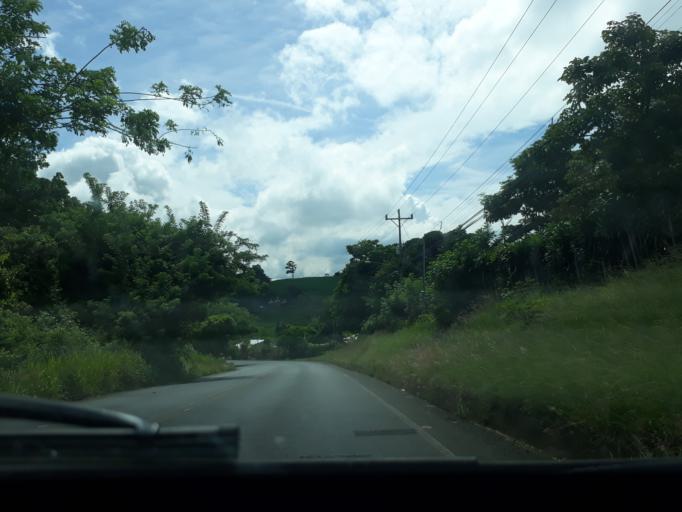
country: CR
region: Alajuela
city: Atenas
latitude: 10.0359
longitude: -84.3519
